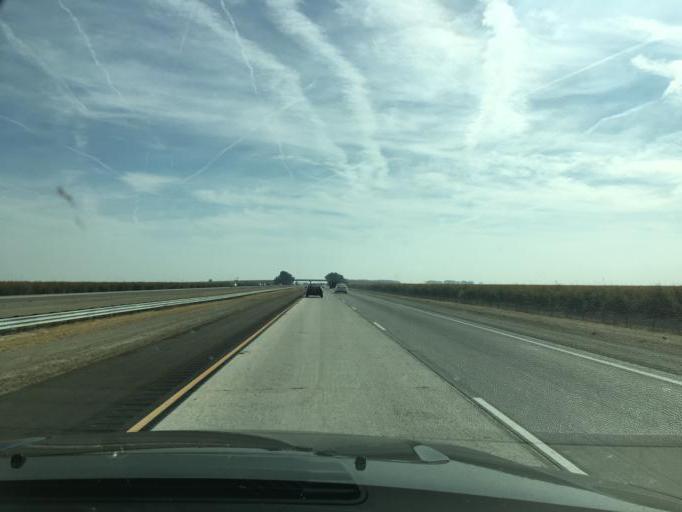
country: US
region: California
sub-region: Kern County
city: Lost Hills
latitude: 35.5825
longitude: -119.6233
